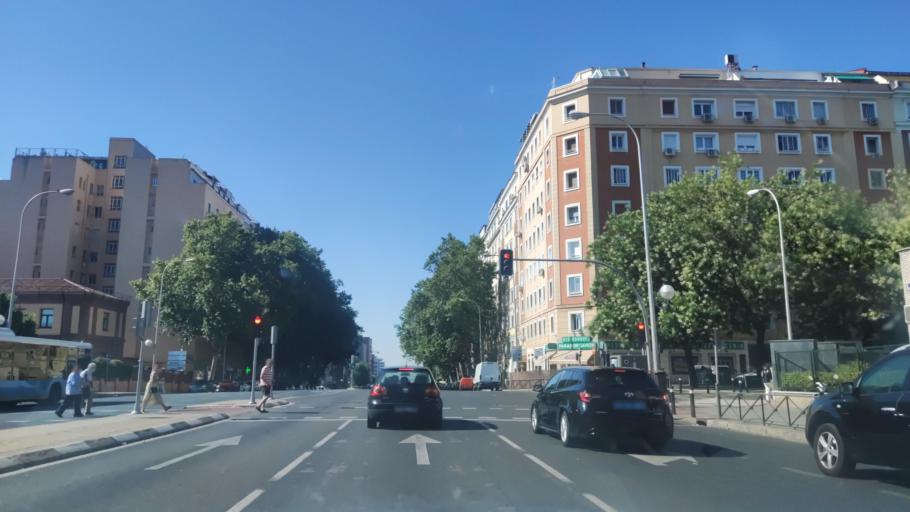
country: ES
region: Madrid
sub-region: Provincia de Madrid
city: Retiro
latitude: 40.4184
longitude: -3.6693
